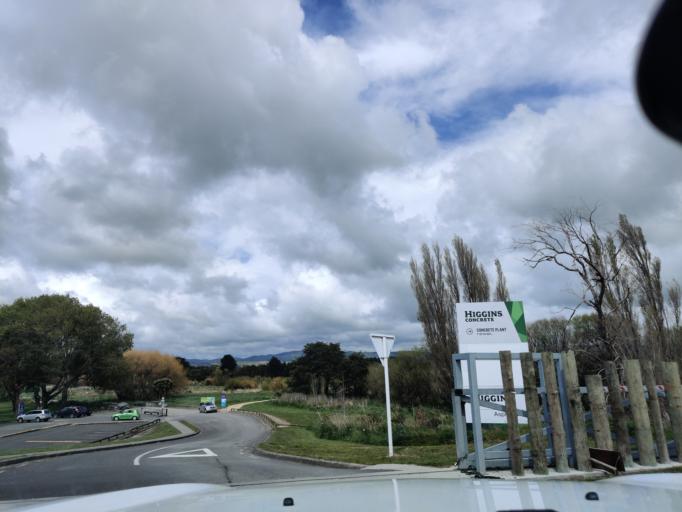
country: NZ
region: Manawatu-Wanganui
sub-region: Palmerston North City
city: Palmerston North
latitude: -40.3823
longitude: 175.5868
